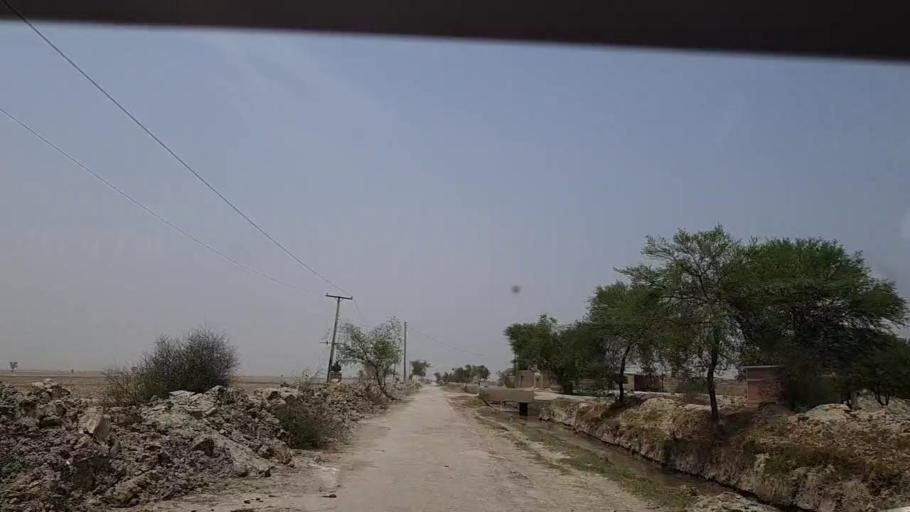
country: PK
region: Sindh
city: Khairpur Nathan Shah
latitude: 27.0461
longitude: 67.6189
